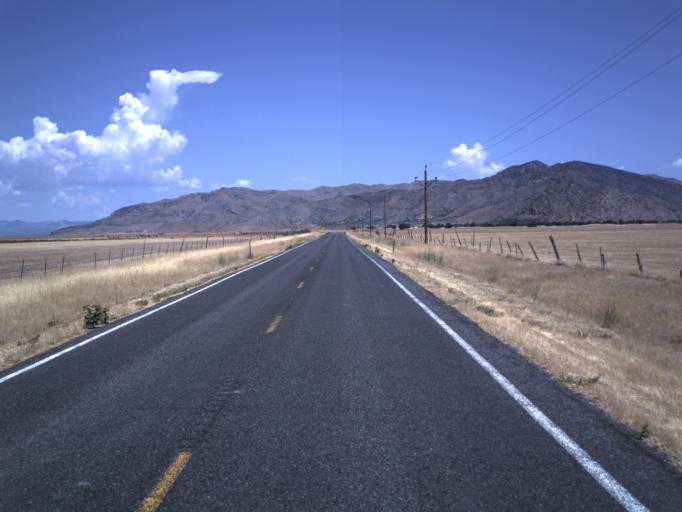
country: US
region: Utah
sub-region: Millard County
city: Delta
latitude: 39.5036
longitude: -112.2690
